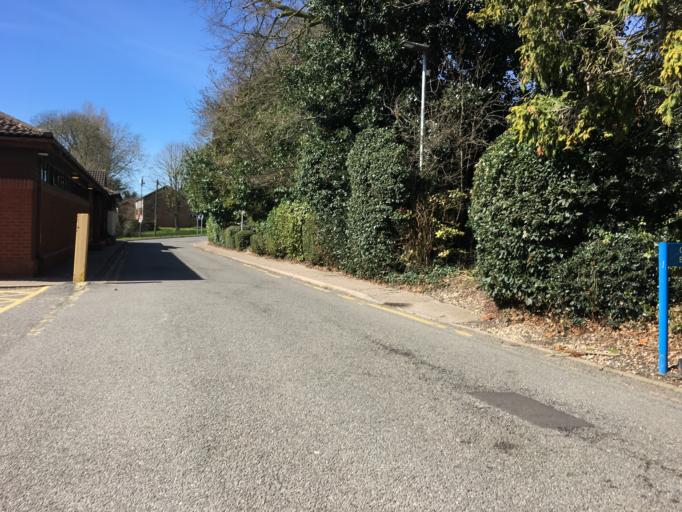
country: GB
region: England
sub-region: Warwickshire
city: Rugby
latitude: 52.3655
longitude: -1.2595
